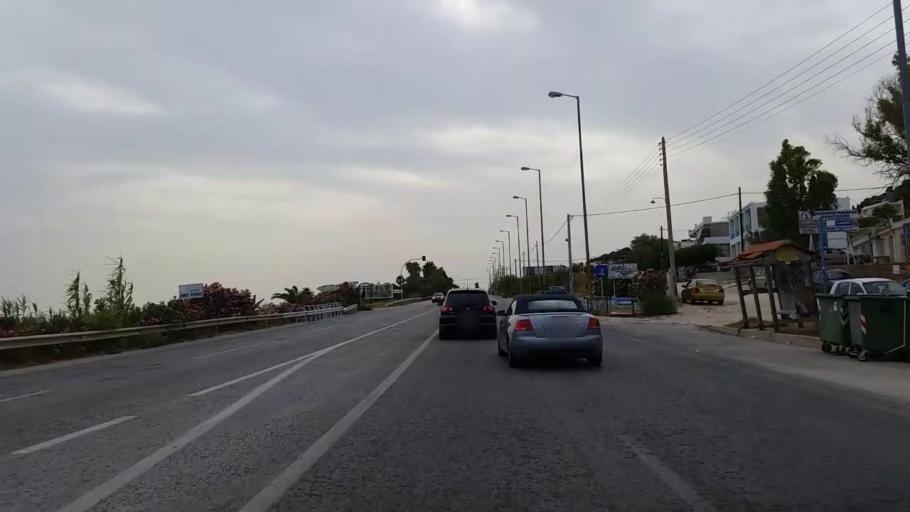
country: GR
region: Attica
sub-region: Nomarchia Anatolikis Attikis
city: Agios Dimitrios Kropias
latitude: 37.8027
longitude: 23.8656
